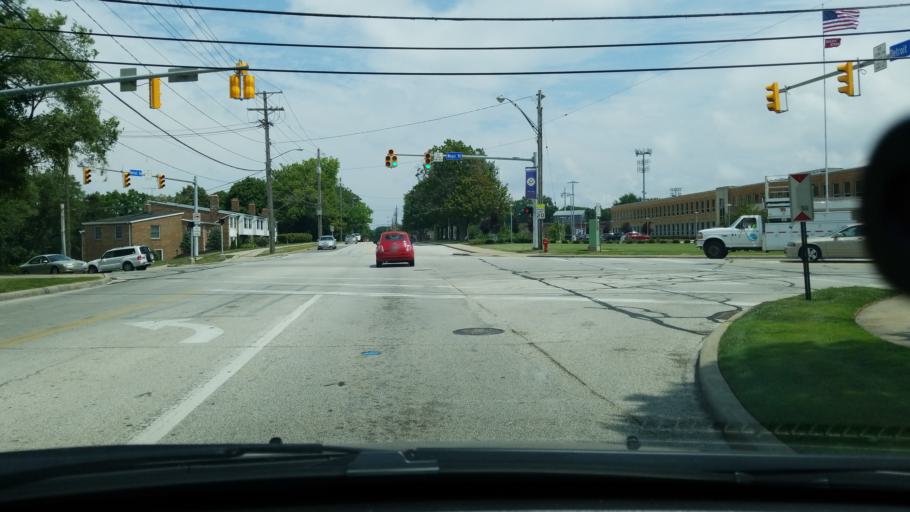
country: US
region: Ohio
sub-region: Cuyahoga County
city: Rocky River
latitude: 41.4743
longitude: -81.8528
